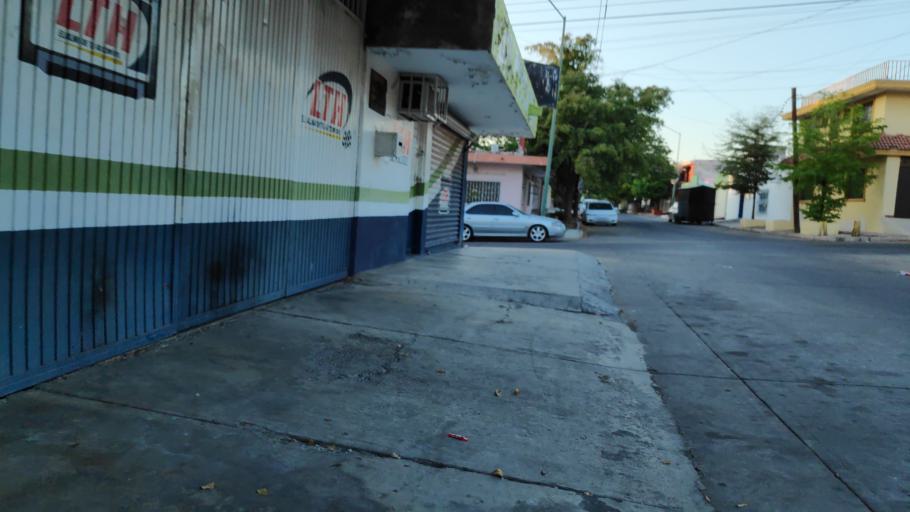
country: MX
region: Sinaloa
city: Culiacan
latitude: 24.7882
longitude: -107.4029
